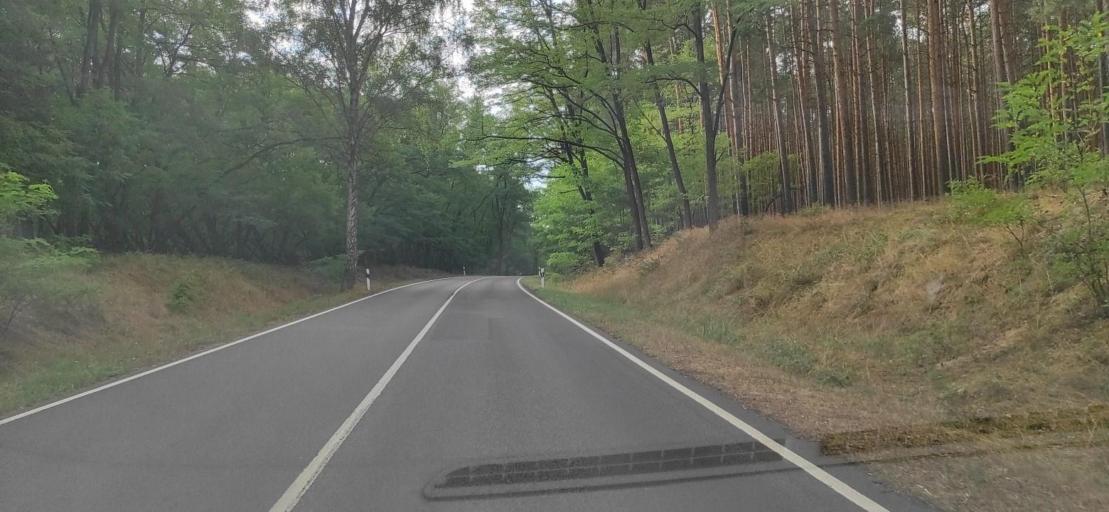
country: DE
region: Brandenburg
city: Forst
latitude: 51.6847
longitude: 14.7211
